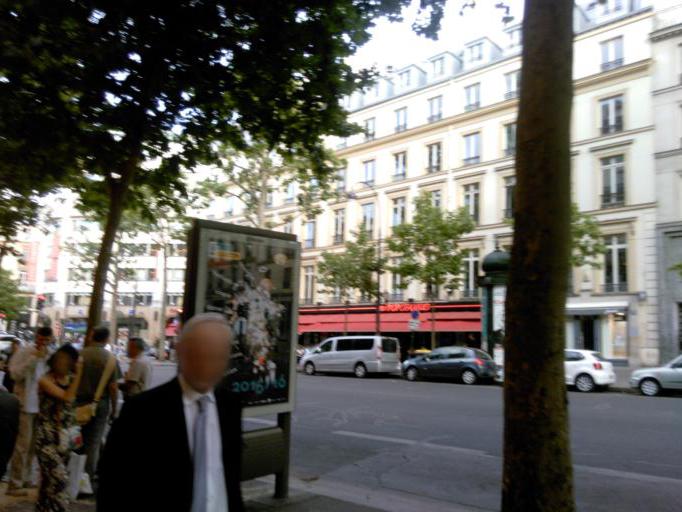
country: FR
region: Ile-de-France
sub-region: Paris
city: Paris
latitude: 48.8709
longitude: 2.3336
